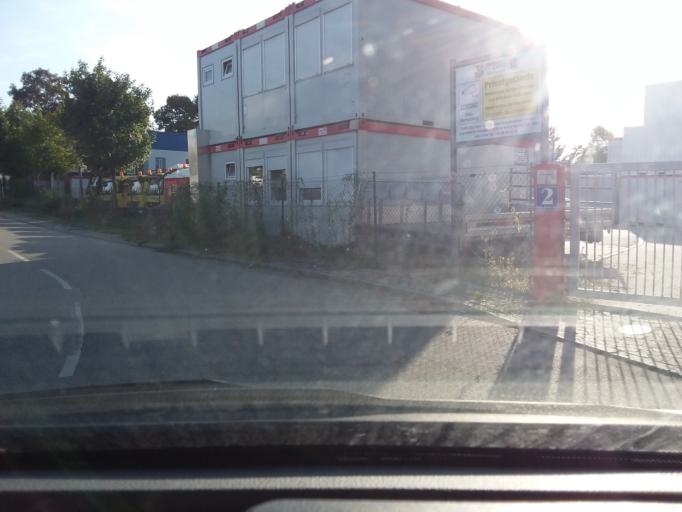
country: DE
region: Bavaria
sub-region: Upper Bavaria
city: Ismaning
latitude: 48.2375
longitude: 11.6822
